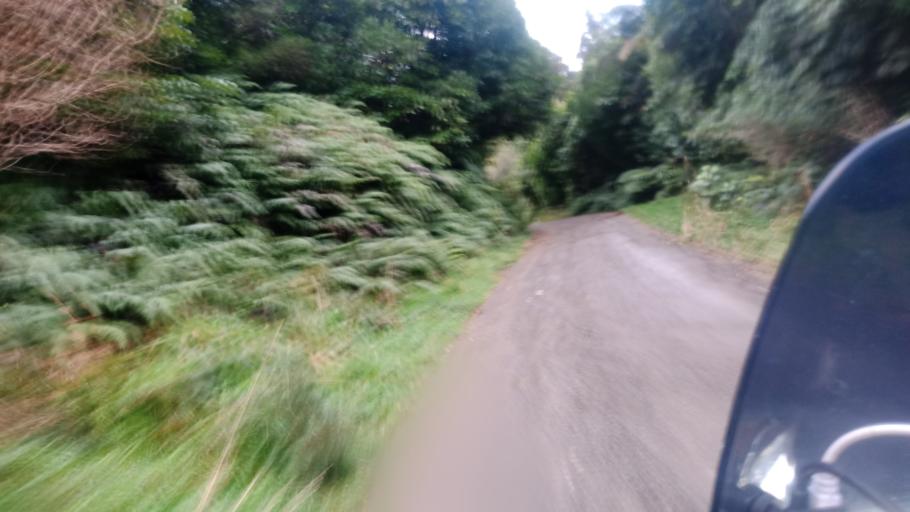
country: NZ
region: Hawke's Bay
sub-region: Wairoa District
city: Wairoa
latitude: -38.7322
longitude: 177.0910
